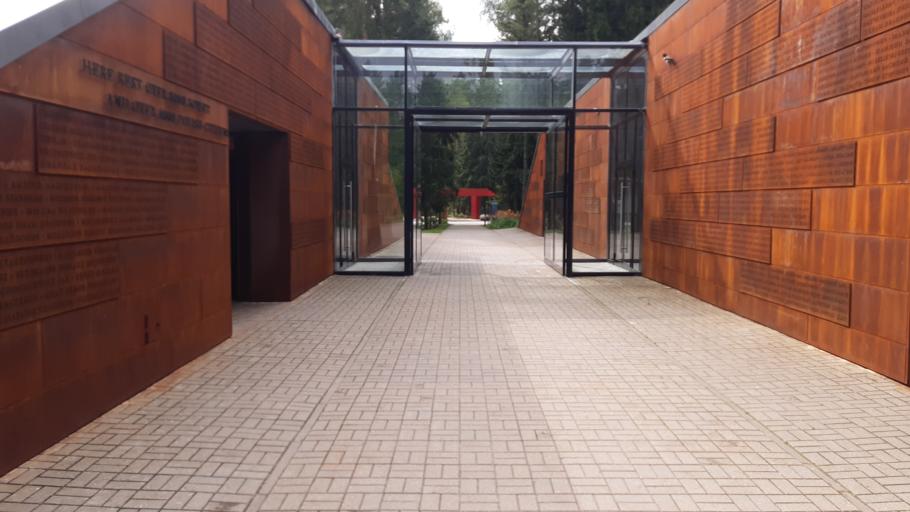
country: RU
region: Smolensk
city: Katyn'
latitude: 54.7755
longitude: 31.7884
